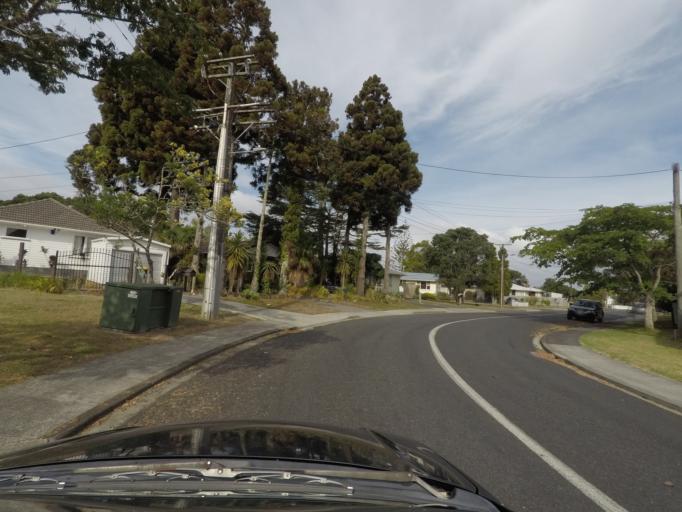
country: NZ
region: Auckland
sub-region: Auckland
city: Rosebank
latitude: -36.8904
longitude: 174.6674
